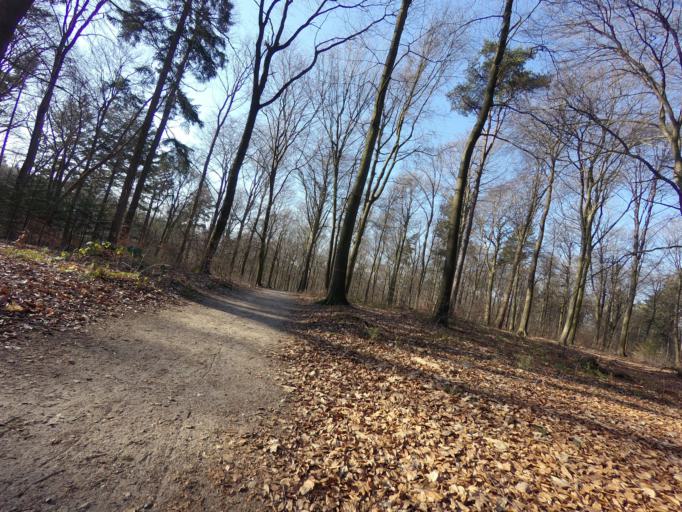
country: NL
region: Gelderland
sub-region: Gemeente Lochem
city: Barchem
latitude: 52.1415
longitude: 6.4280
